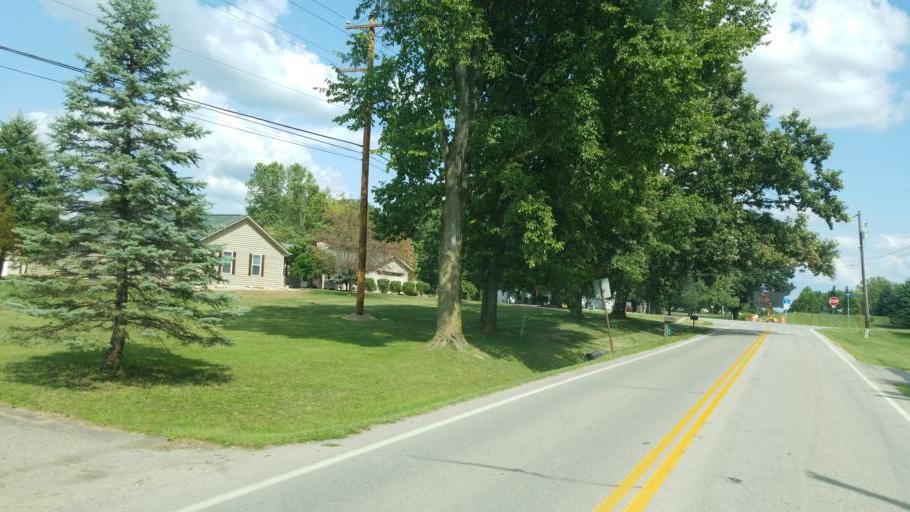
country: US
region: Ohio
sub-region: Delaware County
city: Lewis Center
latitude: 40.2417
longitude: -83.0430
